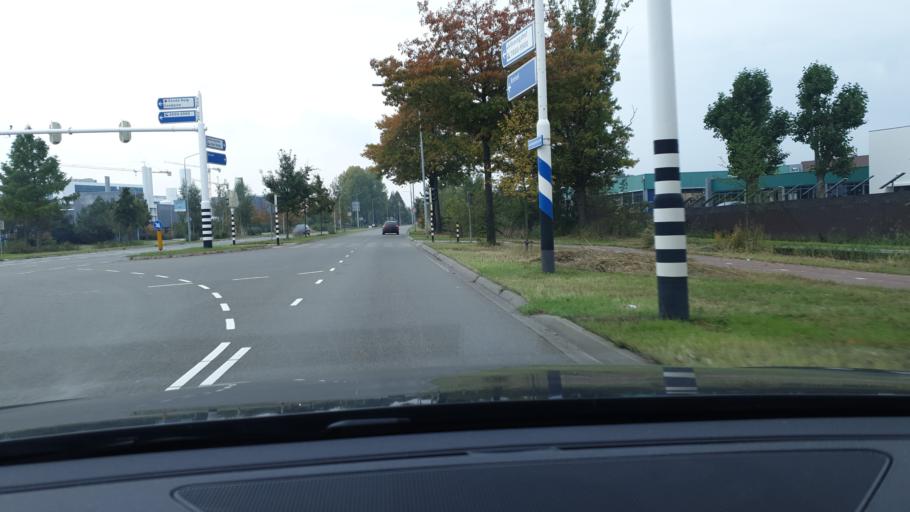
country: NL
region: North Brabant
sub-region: Gemeente Veldhoven
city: Veldhoven
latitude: 51.4070
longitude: 5.4148
